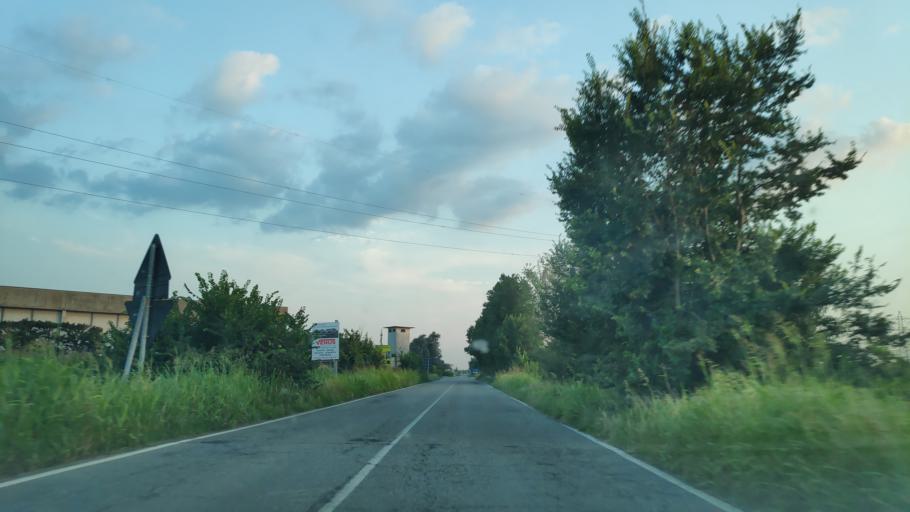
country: IT
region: Lombardy
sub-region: Citta metropolitana di Milano
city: Liscate
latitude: 45.4790
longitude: 9.4258
